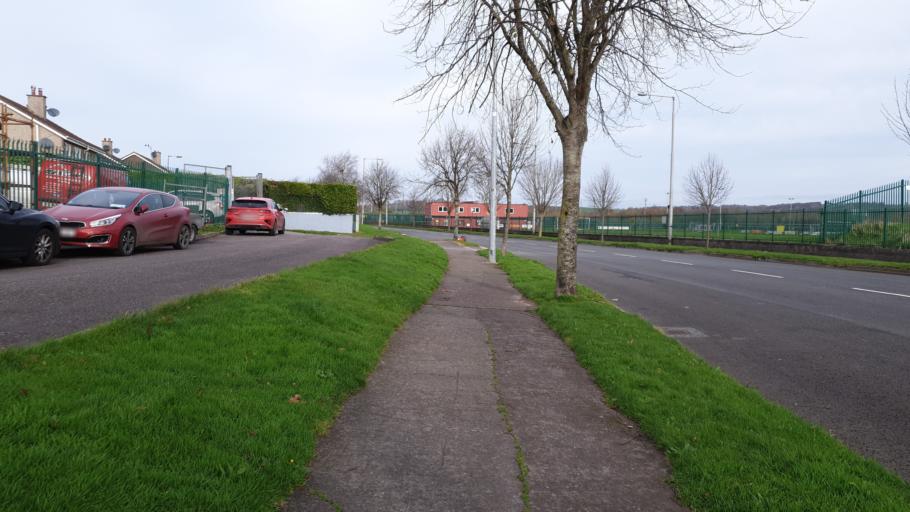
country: IE
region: Munster
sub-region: County Cork
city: Passage West
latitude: 51.8908
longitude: -8.3952
